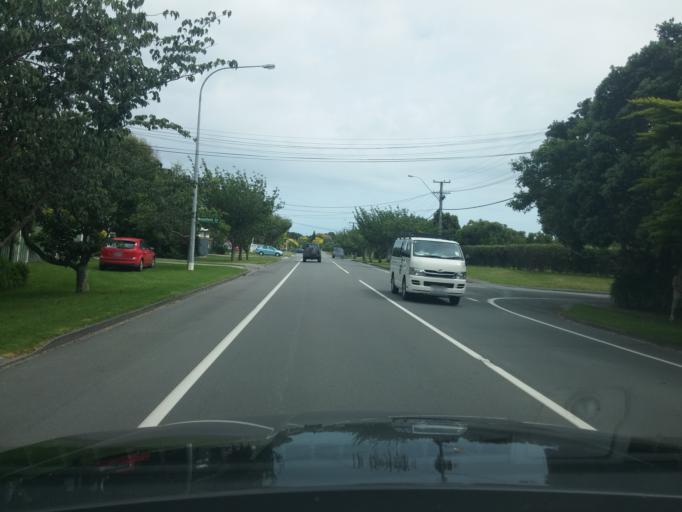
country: NZ
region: Wellington
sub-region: Kapiti Coast District
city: Paraparaumu
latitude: -40.8769
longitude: 175.0440
